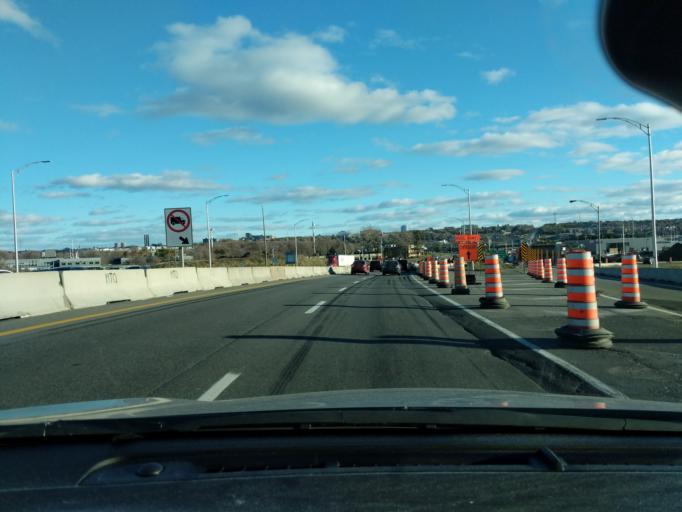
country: CA
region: Quebec
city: L'Ancienne-Lorette
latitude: 46.7963
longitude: -71.3183
